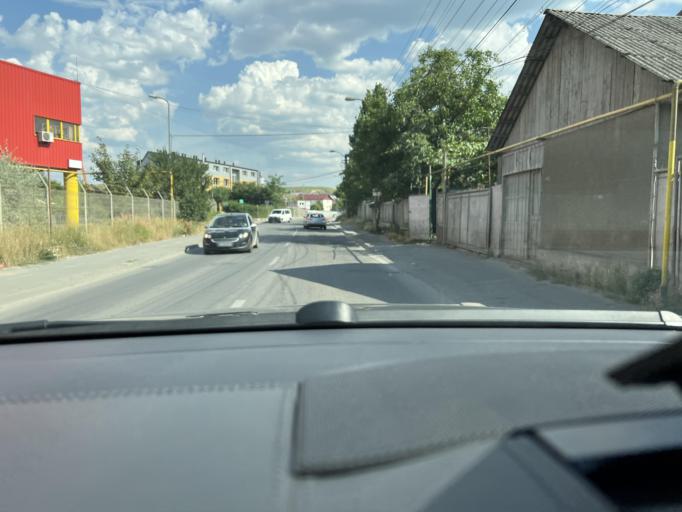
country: RO
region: Cluj
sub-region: Comuna Apahida
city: Dezmir
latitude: 46.7781
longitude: 23.6817
